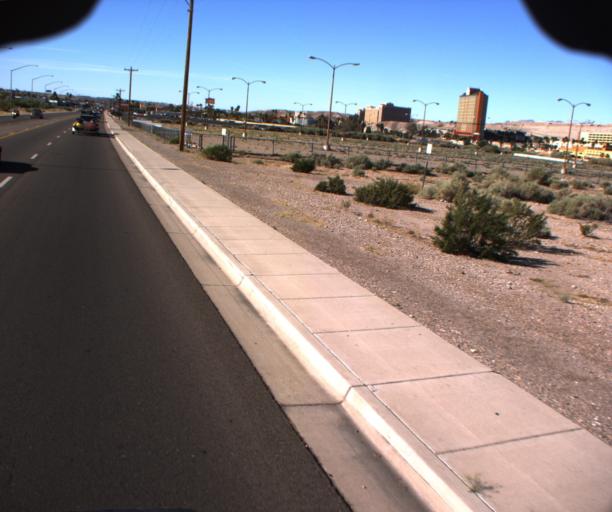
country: US
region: Arizona
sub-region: Mohave County
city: Bullhead City
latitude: 35.1584
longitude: -114.5669
